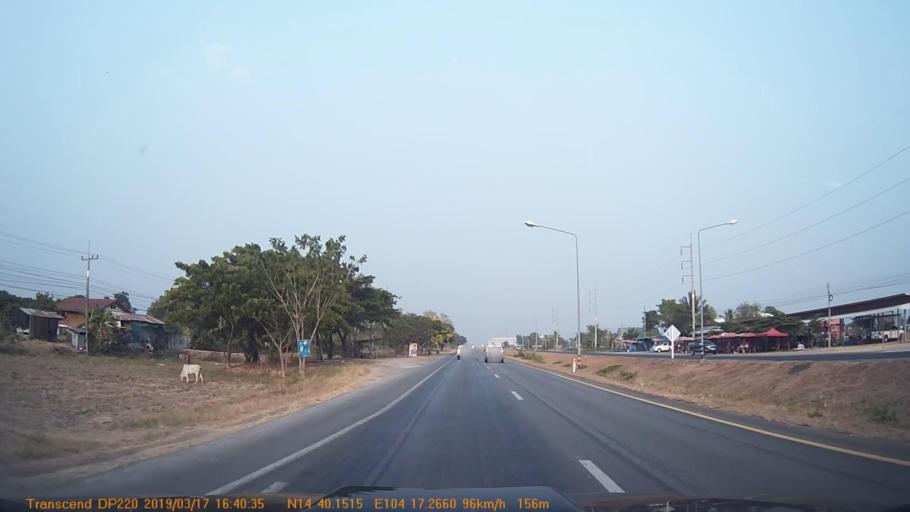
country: TH
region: Sisaket
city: Khu Khan
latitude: 14.6695
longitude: 104.2881
